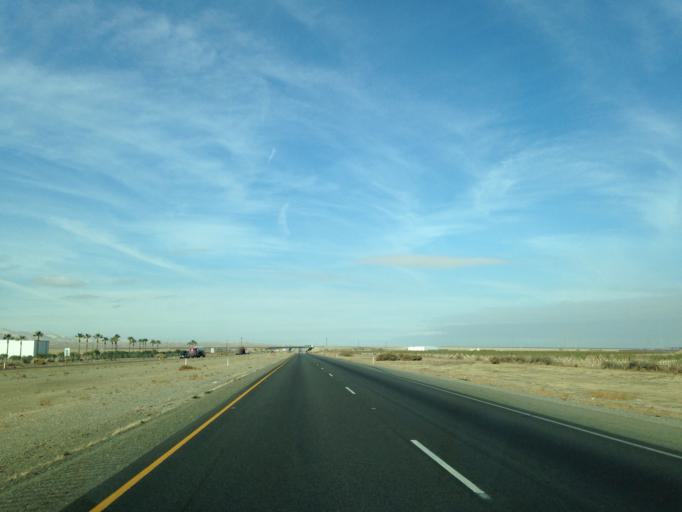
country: US
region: California
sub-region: Fresno County
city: San Joaquin
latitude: 36.4284
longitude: -120.3874
